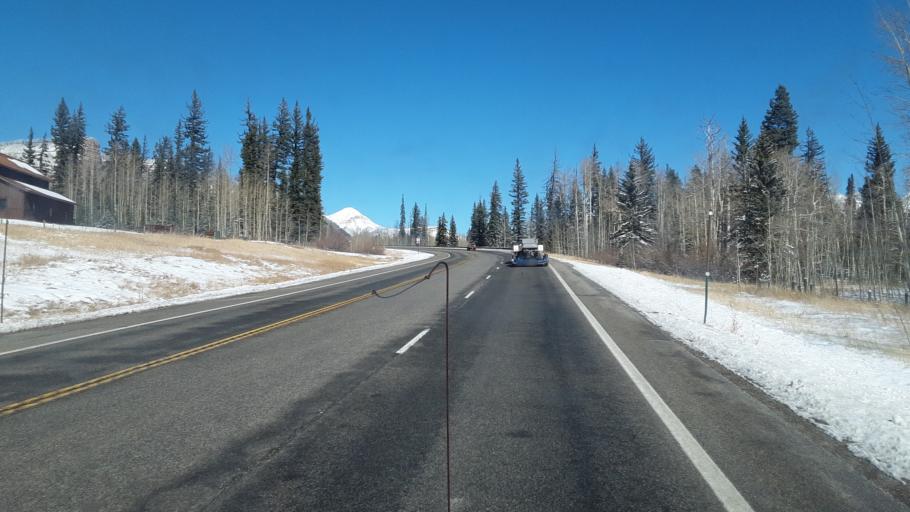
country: US
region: Colorado
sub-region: San Juan County
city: Silverton
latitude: 37.5724
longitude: -107.8231
